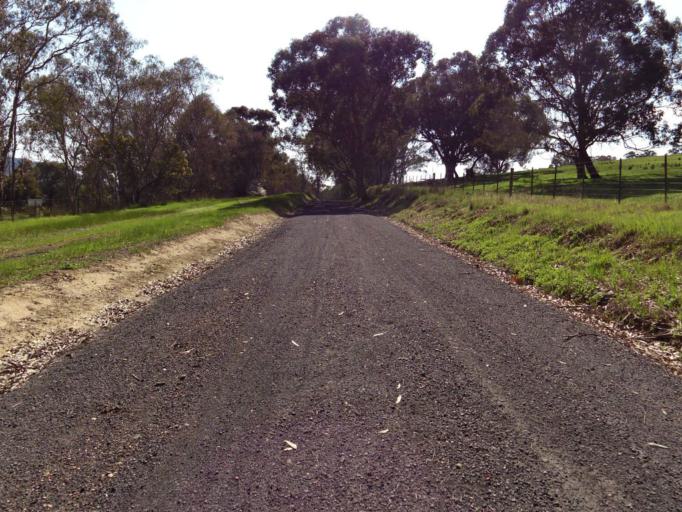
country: AU
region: Victoria
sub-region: Murrindindi
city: Alexandra
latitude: -37.1365
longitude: 145.5916
